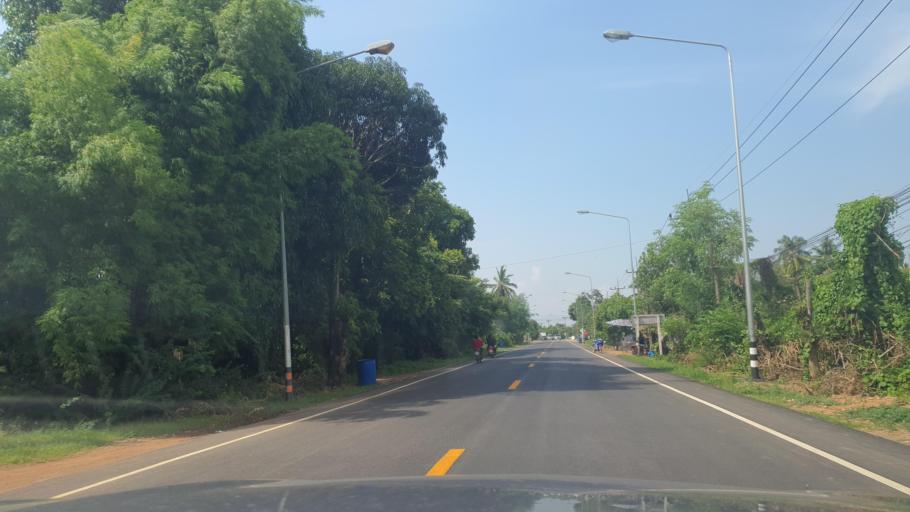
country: TH
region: Sukhothai
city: Si Samrong
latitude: 17.1633
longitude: 99.8305
